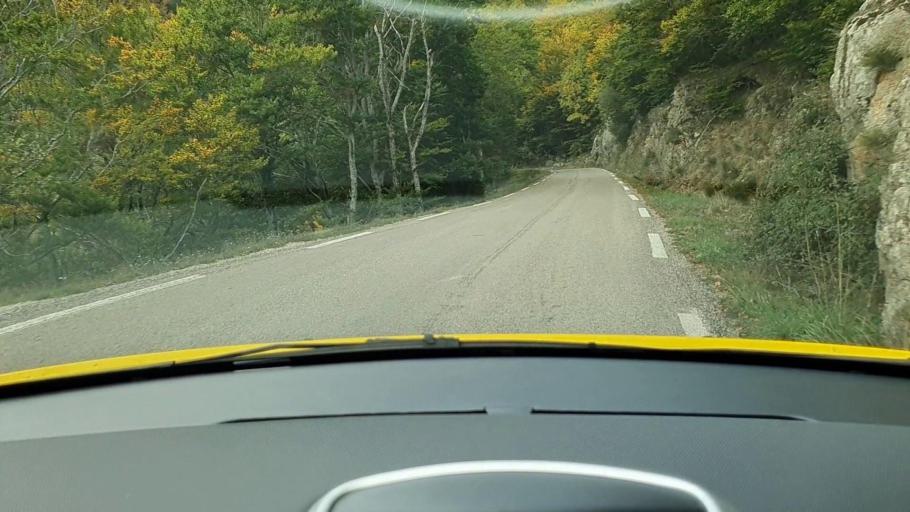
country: FR
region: Languedoc-Roussillon
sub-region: Departement du Gard
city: Le Vigan
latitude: 44.0402
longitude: 3.5651
